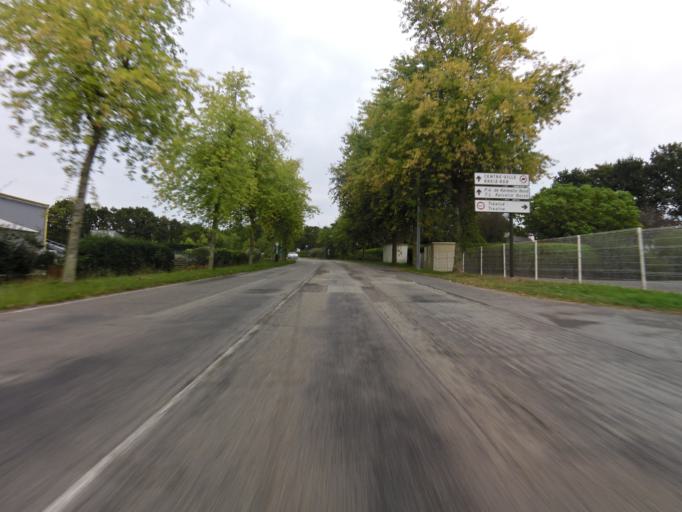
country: FR
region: Brittany
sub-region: Departement du Morbihan
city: Saint-Ave
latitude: 47.6780
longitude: -2.7306
